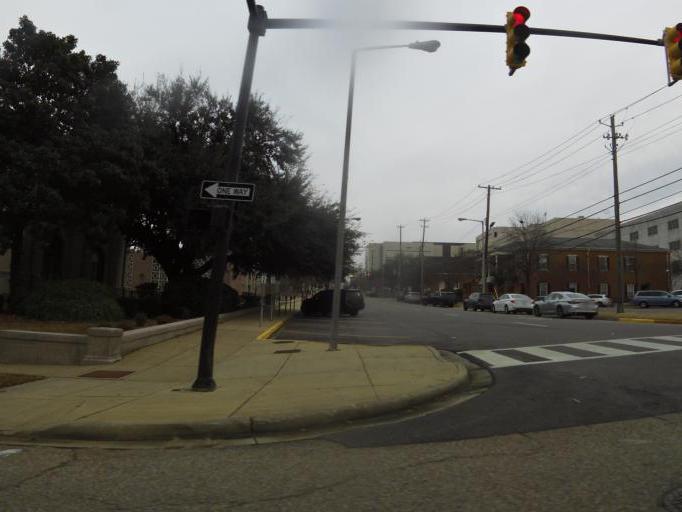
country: US
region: Alabama
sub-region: Montgomery County
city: Montgomery
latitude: 32.3752
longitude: -86.3073
